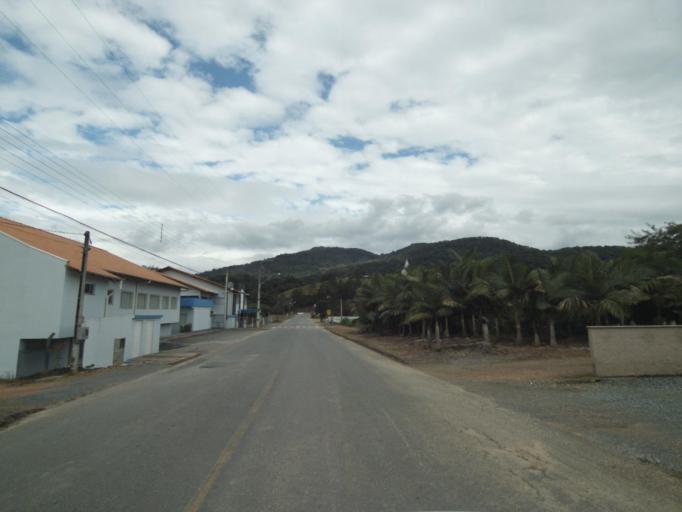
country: BR
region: Santa Catarina
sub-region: Pomerode
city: Pomerode
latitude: -26.7207
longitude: -49.2043
